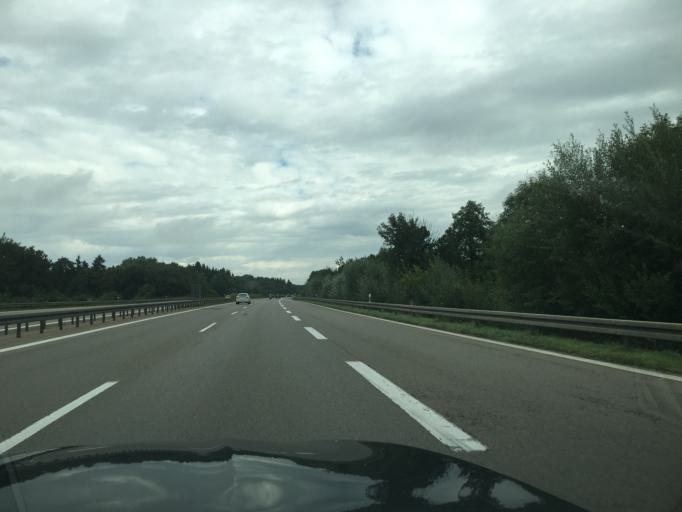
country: DE
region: Bavaria
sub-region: Swabia
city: Nersingen
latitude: 48.4190
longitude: 10.0950
